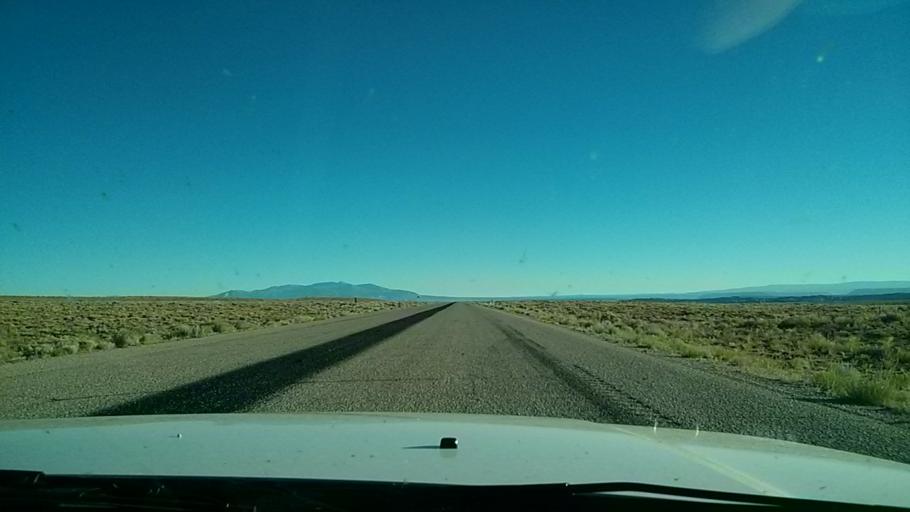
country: US
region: Utah
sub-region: Emery County
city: Ferron
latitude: 38.5668
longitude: -110.6066
